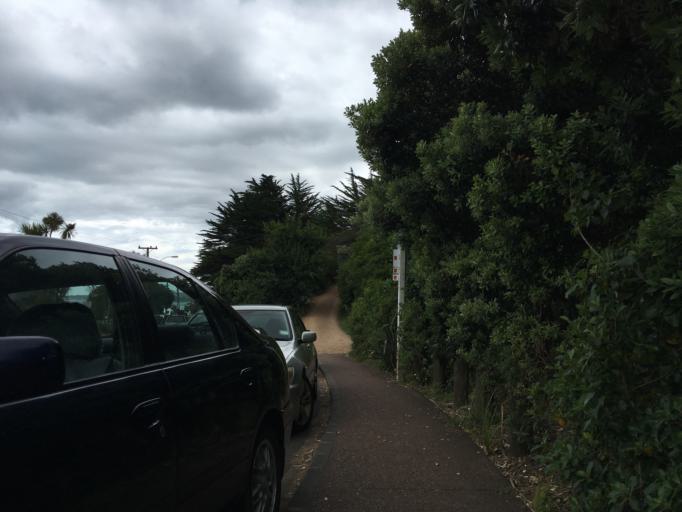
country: NZ
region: Auckland
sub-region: Auckland
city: Pakuranga
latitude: -36.7808
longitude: 174.9951
